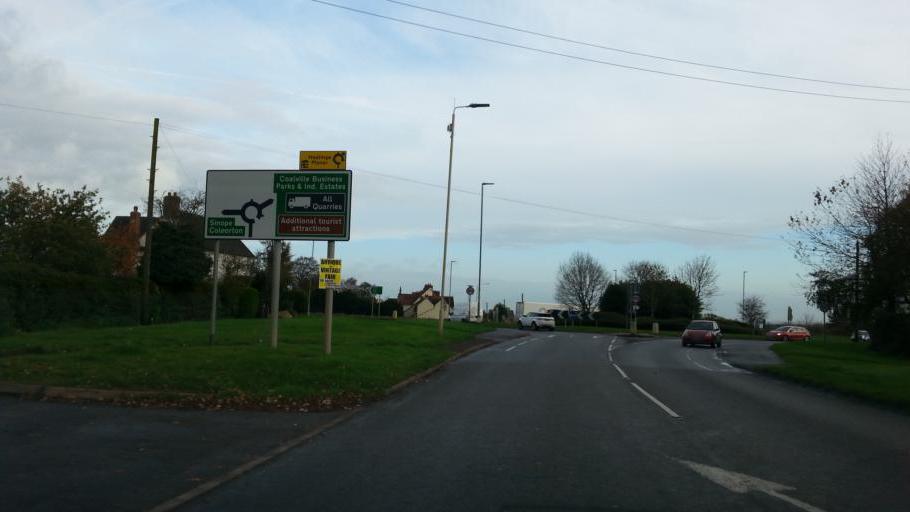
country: GB
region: England
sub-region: Leicestershire
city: Coalville
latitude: 52.7307
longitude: -1.3953
